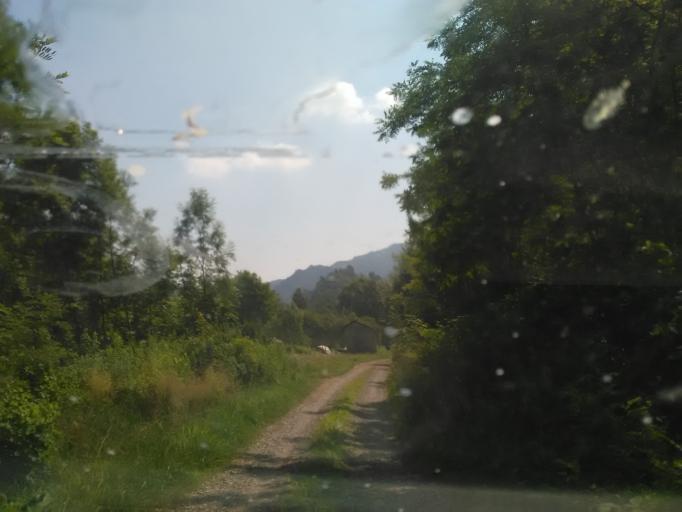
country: IT
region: Piedmont
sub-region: Provincia di Biella
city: Crevacuore
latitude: 45.6830
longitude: 8.2327
